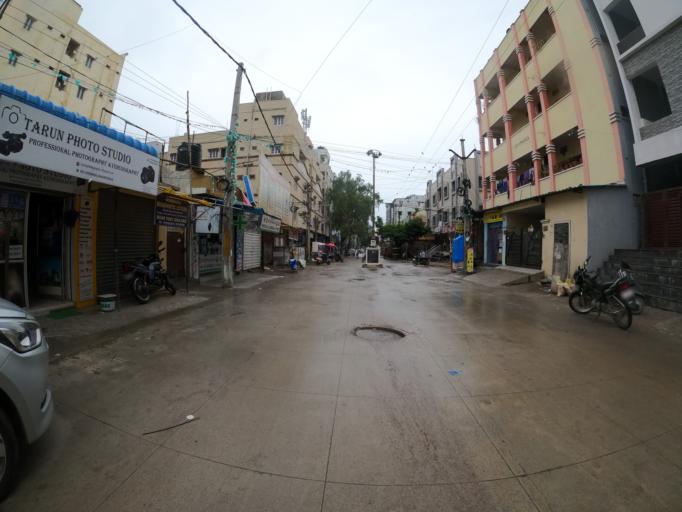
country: IN
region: Telangana
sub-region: Rangareddi
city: Kukatpalli
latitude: 17.4601
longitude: 78.3996
